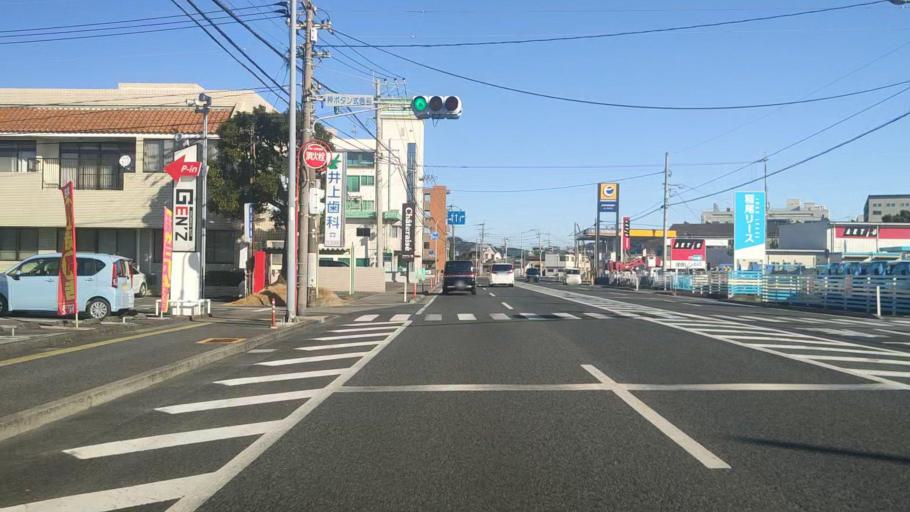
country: JP
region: Miyazaki
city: Nobeoka
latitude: 32.5946
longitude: 131.6767
